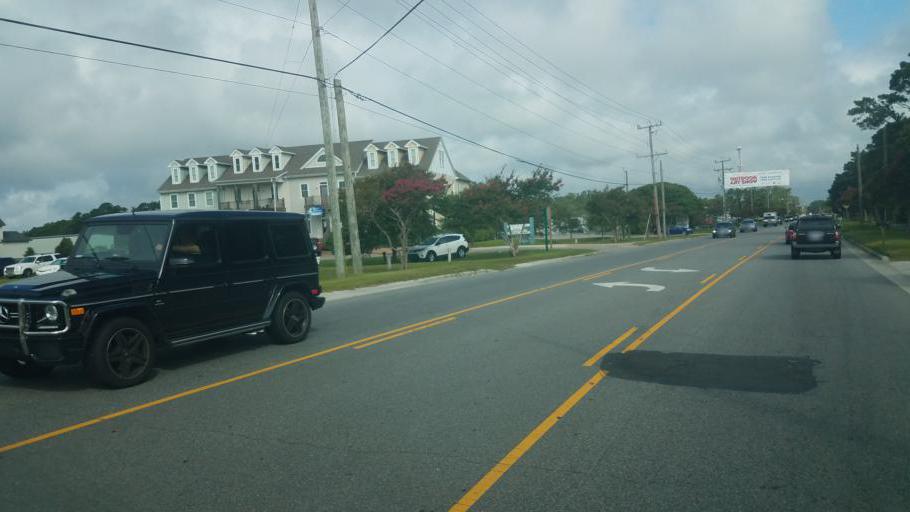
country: US
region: North Carolina
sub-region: Dare County
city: Manteo
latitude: 35.8939
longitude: -75.6656
